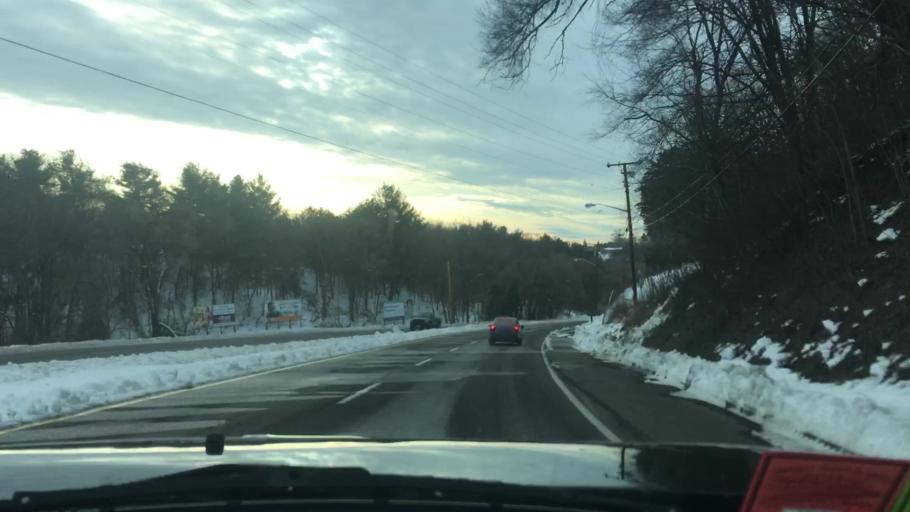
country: US
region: Virginia
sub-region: Pulaski County
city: Pulaski
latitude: 37.0638
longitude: -80.7665
